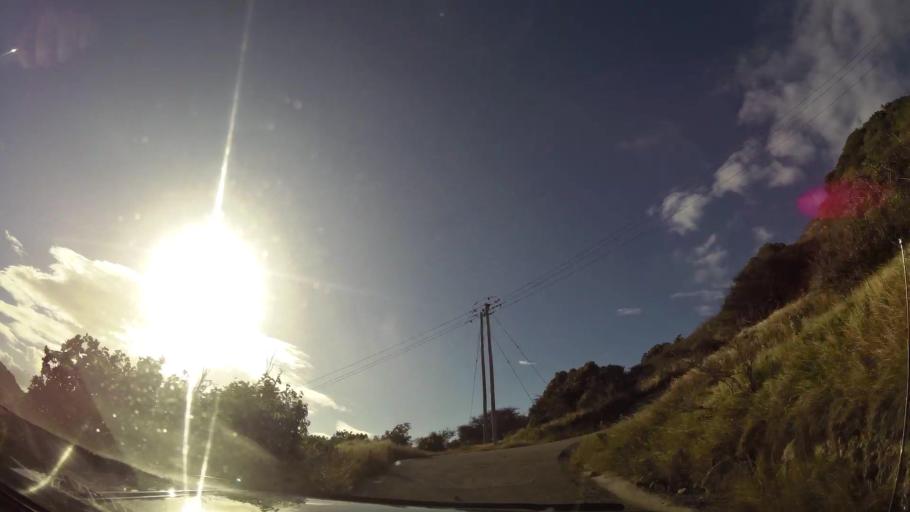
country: MS
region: Saint Peter
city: Brades
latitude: 16.8101
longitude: -62.1925
